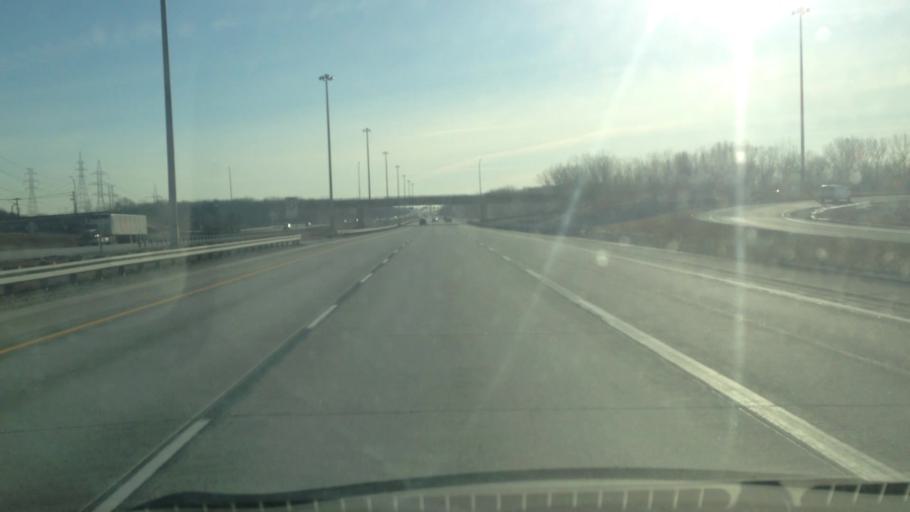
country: CA
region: Quebec
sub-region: Laurentides
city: Boisbriand
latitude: 45.5914
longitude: -73.8494
